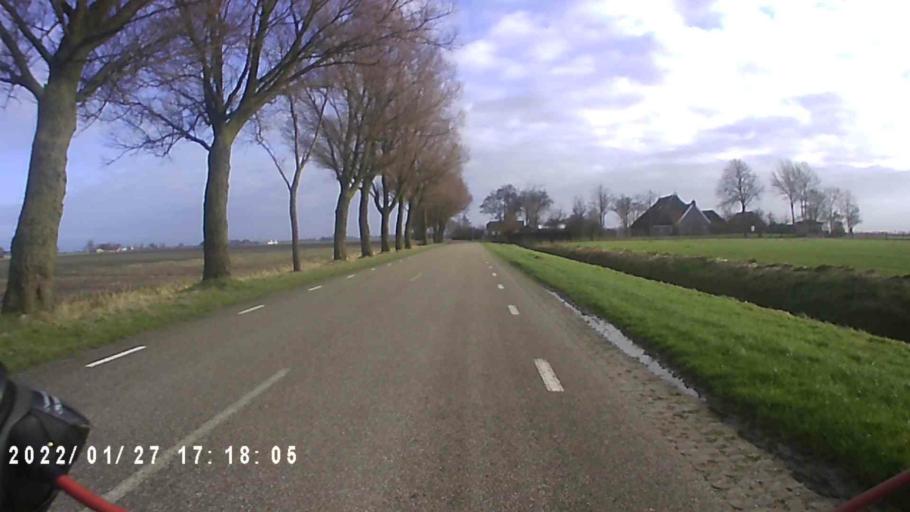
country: NL
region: Friesland
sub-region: Gemeente Dongeradeel
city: Anjum
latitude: 53.3900
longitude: 6.1034
